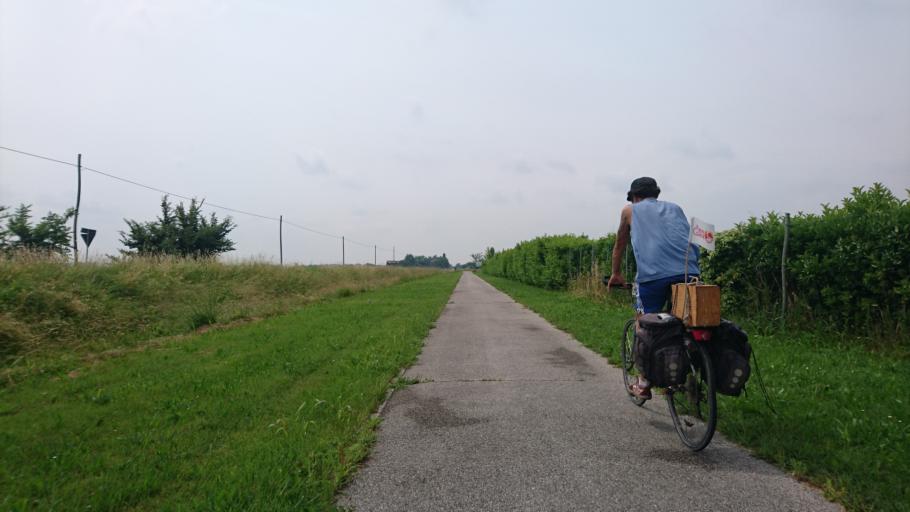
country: IT
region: Veneto
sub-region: Provincia di Padova
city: Vighizzolo d'Este
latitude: 45.1276
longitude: 11.6251
